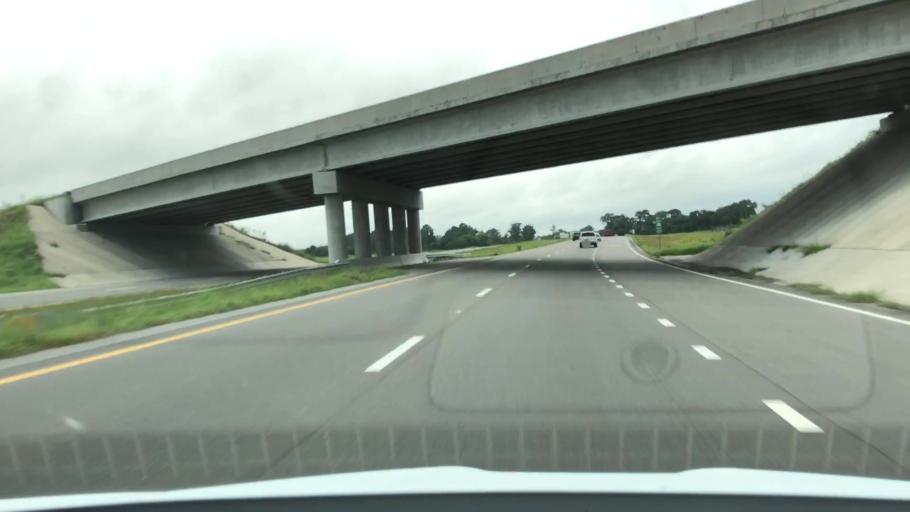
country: US
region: North Carolina
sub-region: Lenoir County
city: La Grange
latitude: 35.3037
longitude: -77.8185
